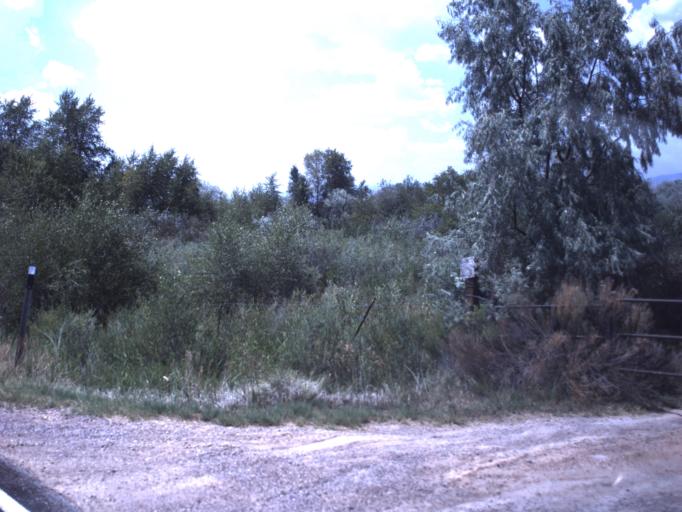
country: US
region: Utah
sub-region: Duchesne County
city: Roosevelt
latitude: 40.4038
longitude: -109.9067
